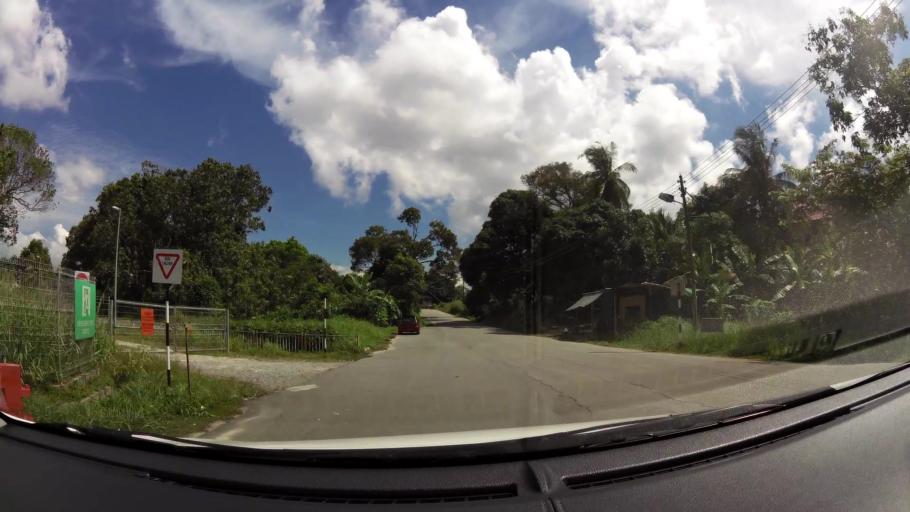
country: BN
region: Brunei and Muara
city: Bandar Seri Begawan
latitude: 4.9734
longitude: 114.9412
